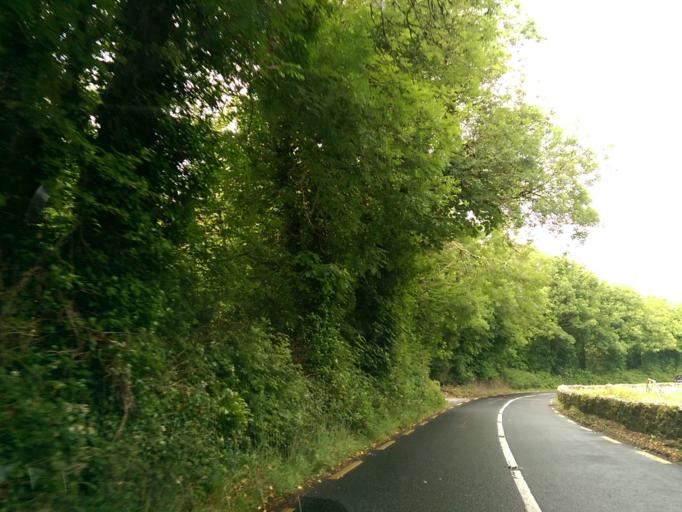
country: IE
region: Connaught
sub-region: County Galway
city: Bearna
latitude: 53.0777
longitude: -9.1861
